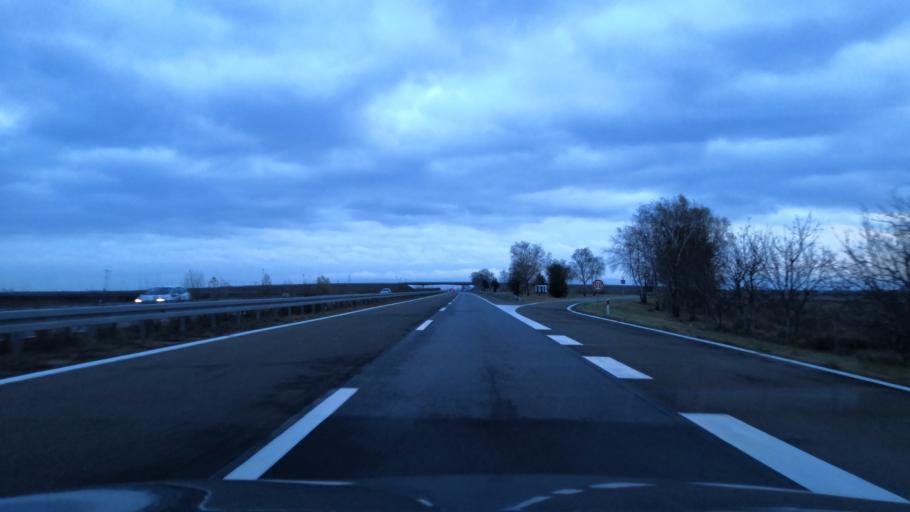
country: RS
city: Kisac
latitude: 45.3653
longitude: 19.7518
